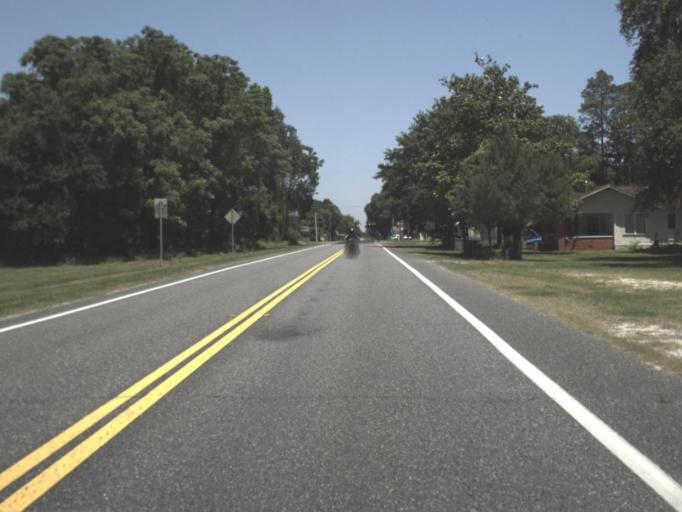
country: US
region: Florida
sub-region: Columbia County
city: Watertown
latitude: 30.2041
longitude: -82.4322
